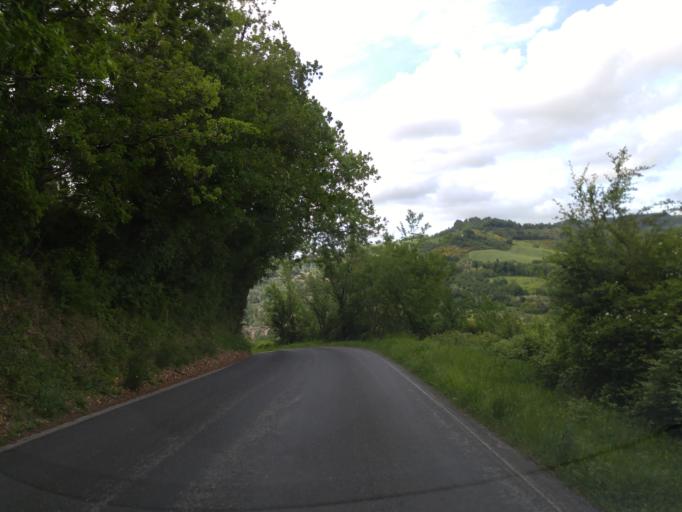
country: IT
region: The Marches
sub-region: Provincia di Pesaro e Urbino
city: Fermignano
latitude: 43.7012
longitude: 12.6374
